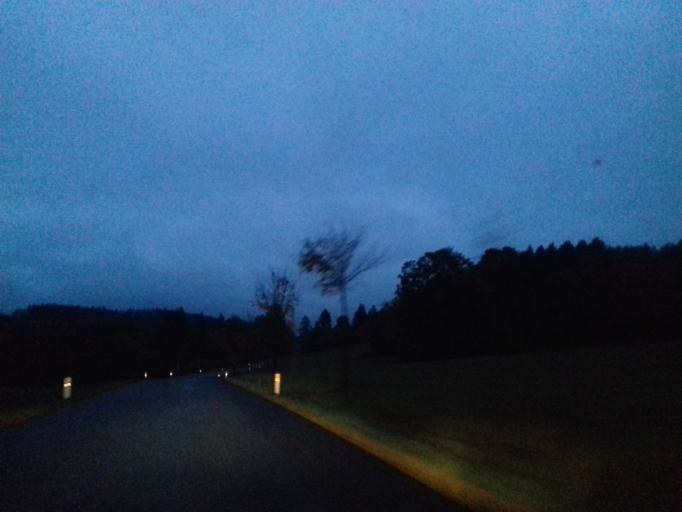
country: CZ
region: South Moravian
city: Olesnice
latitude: 49.5823
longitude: 16.3866
